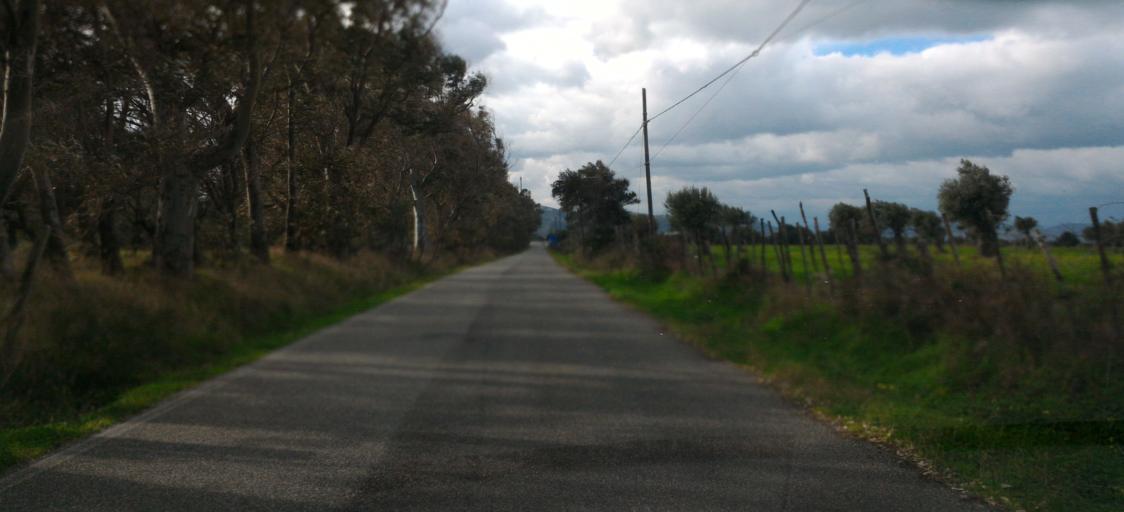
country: IT
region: Calabria
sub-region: Provincia di Crotone
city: Ciro Marina
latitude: 39.4011
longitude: 17.1214
